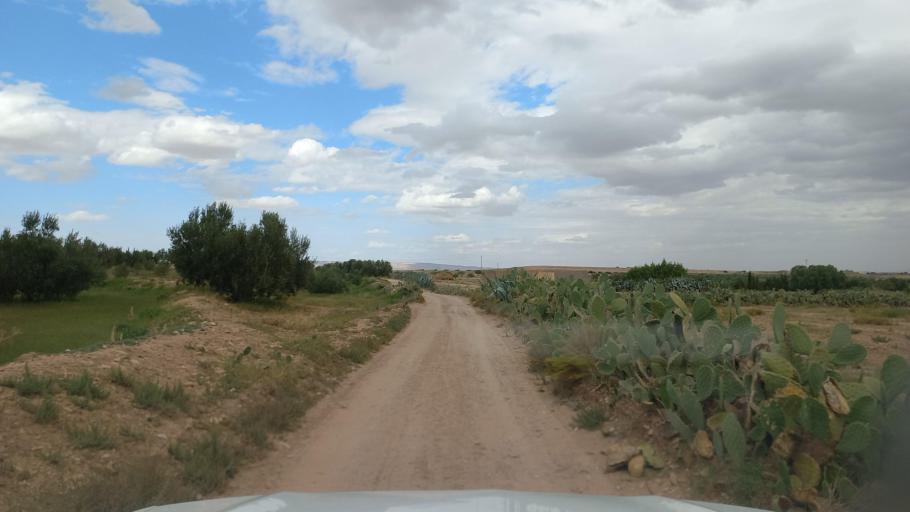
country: TN
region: Al Qasrayn
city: Sbiba
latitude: 35.4380
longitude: 9.0990
